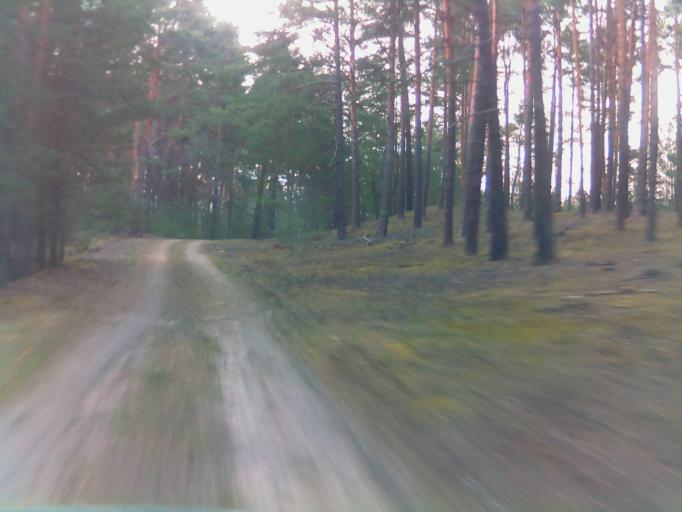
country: DE
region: Brandenburg
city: Jamlitz
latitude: 51.9792
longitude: 14.4118
